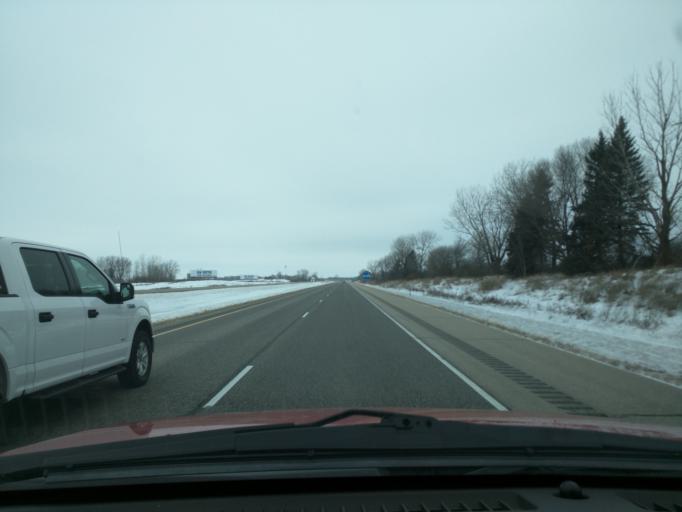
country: US
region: Minnesota
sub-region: Winona County
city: Winona
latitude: 43.9568
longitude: -91.6685
